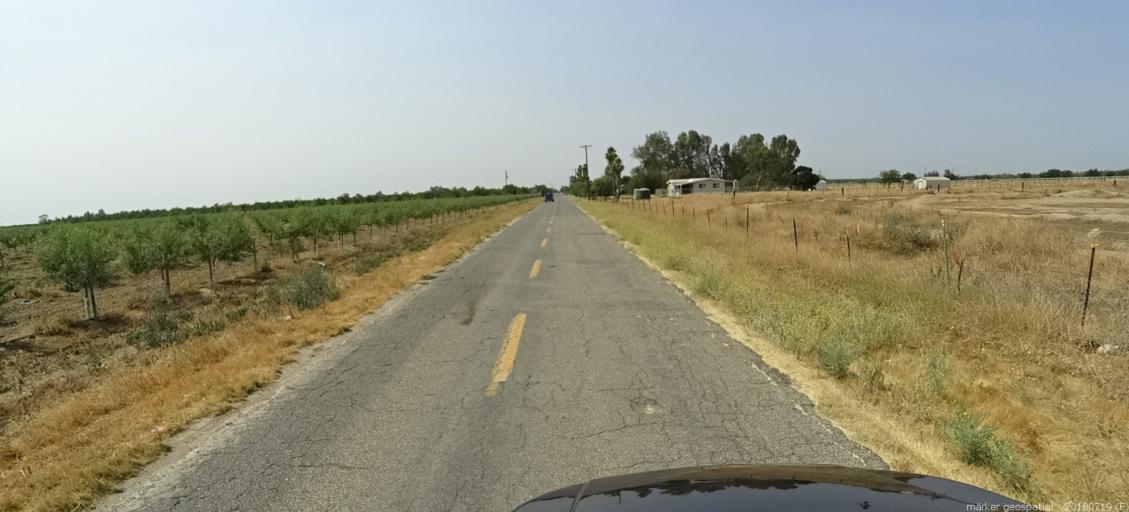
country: US
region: California
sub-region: Madera County
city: Fairmead
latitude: 37.0971
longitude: -120.1930
